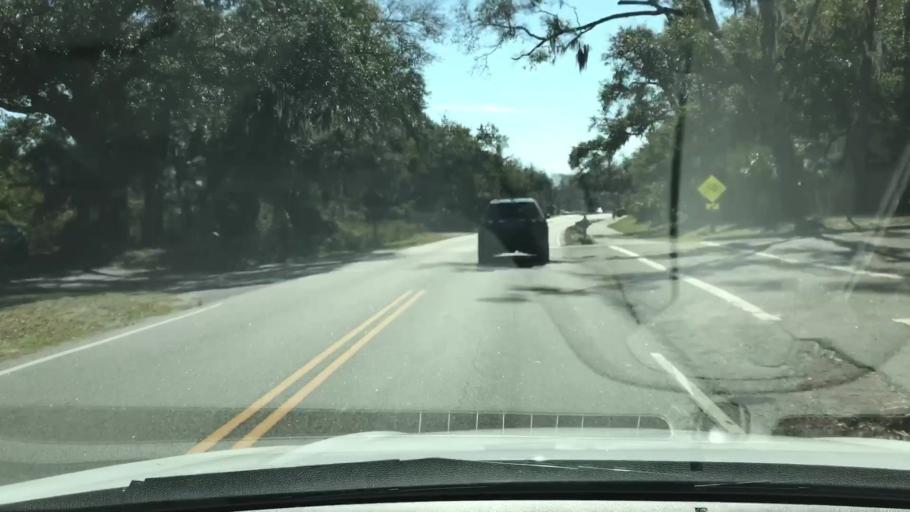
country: US
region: South Carolina
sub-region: Beaufort County
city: Hilton Head Island
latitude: 32.2177
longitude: -80.7031
